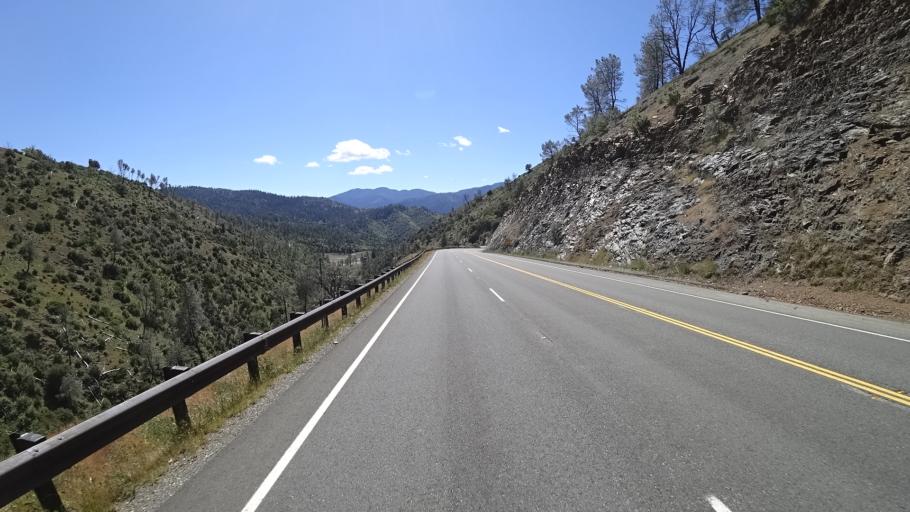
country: US
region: California
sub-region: Trinity County
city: Weaverville
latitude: 40.7416
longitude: -123.0013
